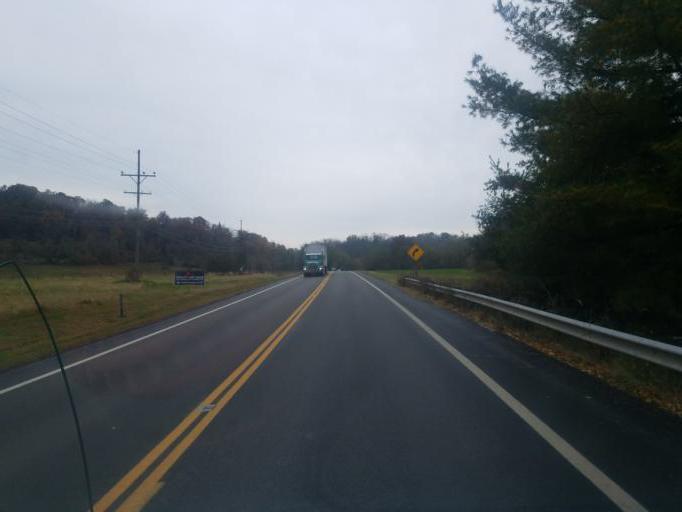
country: US
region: Ohio
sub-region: Washington County
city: Devola
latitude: 39.5231
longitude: -81.4906
